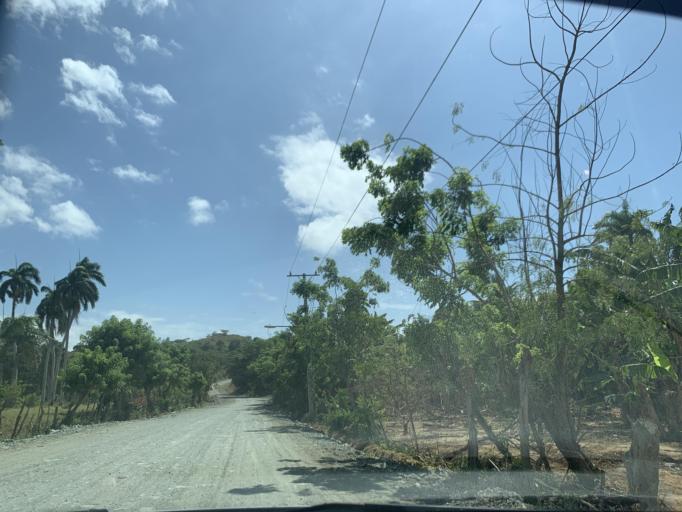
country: DO
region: Puerto Plata
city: Luperon
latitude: 19.8817
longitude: -70.8502
